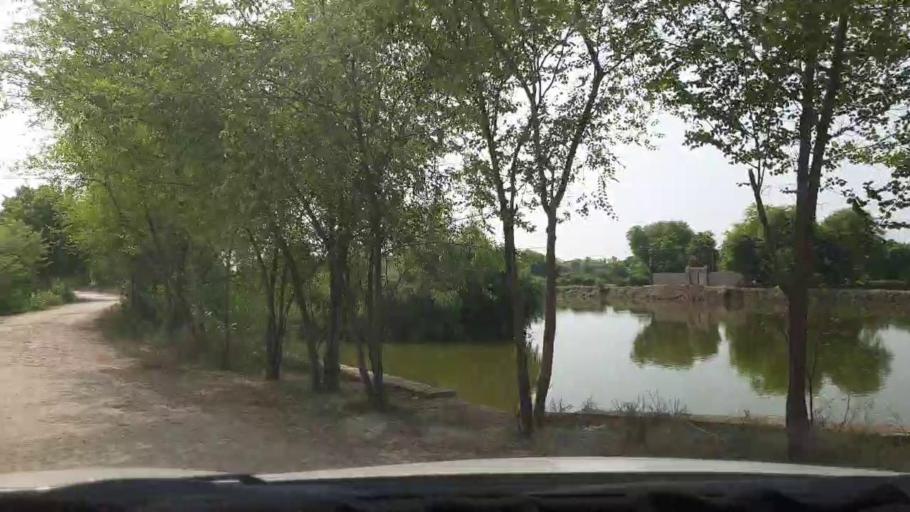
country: PK
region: Sindh
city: Dokri
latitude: 27.3905
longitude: 68.1190
